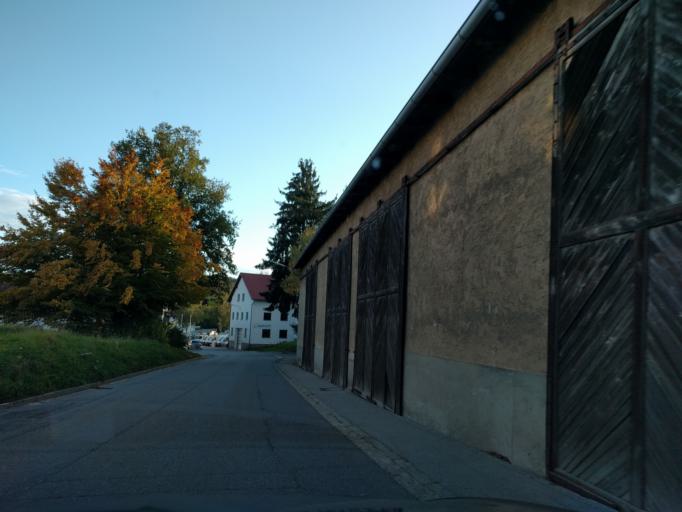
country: DE
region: Bavaria
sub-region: Lower Bavaria
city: Viechtach
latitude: 49.0838
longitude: 12.8845
